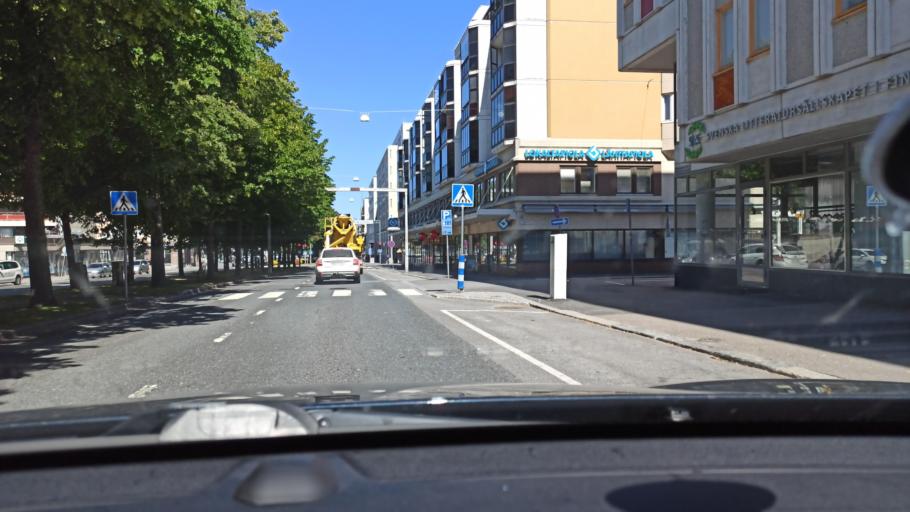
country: FI
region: Ostrobothnia
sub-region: Vaasa
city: Vaasa
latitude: 63.0927
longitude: 21.6188
